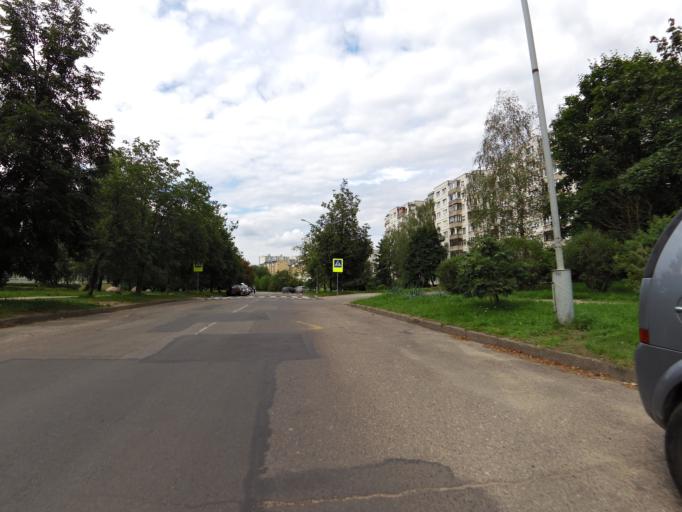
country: LT
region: Vilnius County
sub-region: Vilnius
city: Fabijoniskes
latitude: 54.7186
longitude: 25.2378
